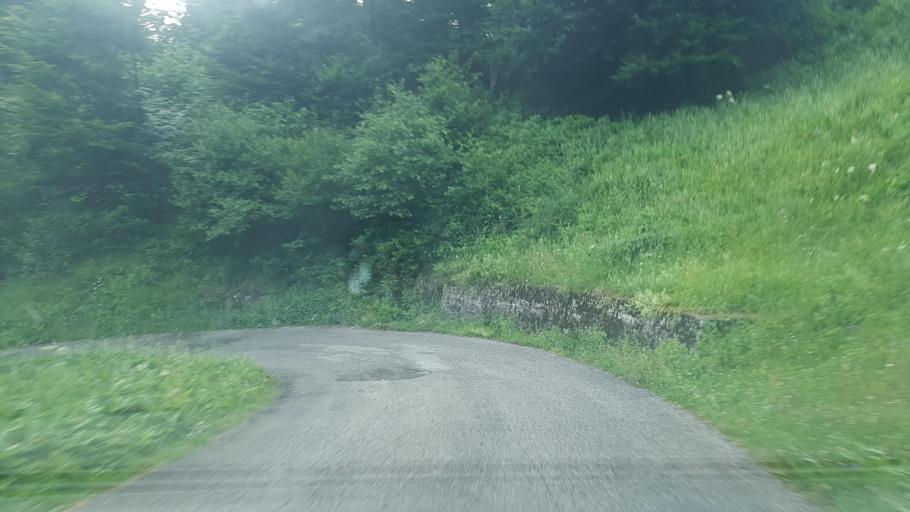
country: IT
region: Friuli Venezia Giulia
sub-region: Provincia di Udine
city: Paularo
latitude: 46.5776
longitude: 13.1138
